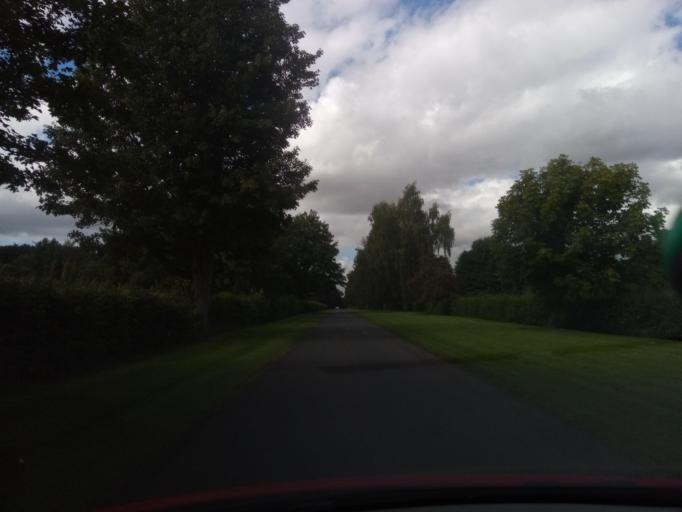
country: GB
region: Scotland
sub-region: The Scottish Borders
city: Coldstream
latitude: 55.6506
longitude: -2.2667
